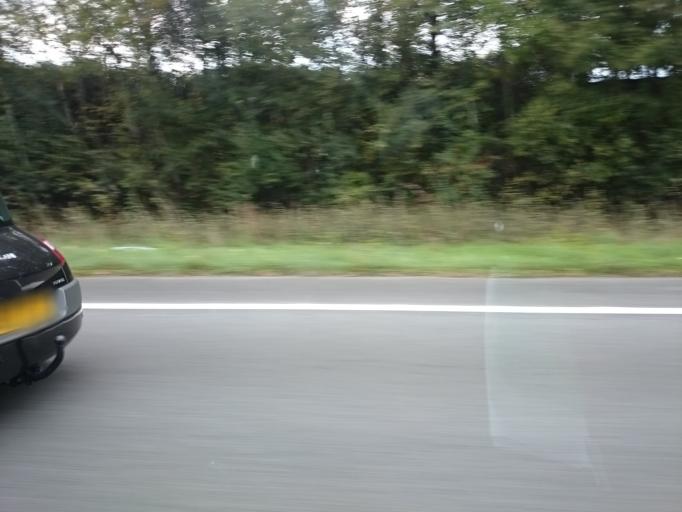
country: FR
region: Pays de la Loire
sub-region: Departement de la Loire-Atlantique
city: Treillieres
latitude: 47.3605
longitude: -1.6561
